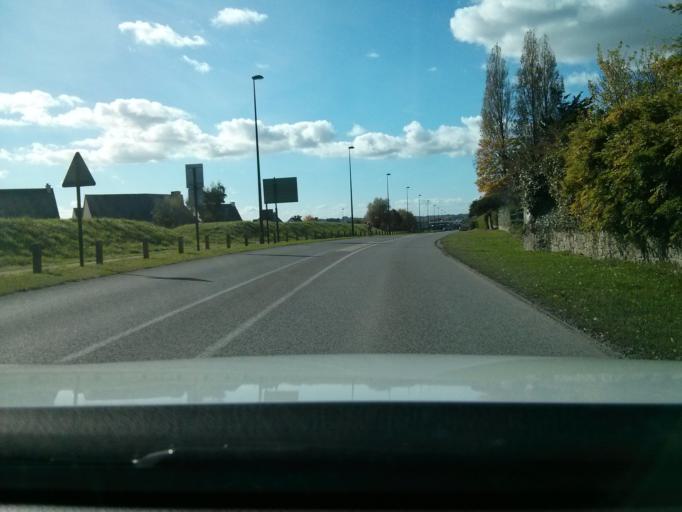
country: FR
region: Brittany
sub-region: Departement des Cotes-d'Armor
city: Ploubalay
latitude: 48.5794
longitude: -2.1453
